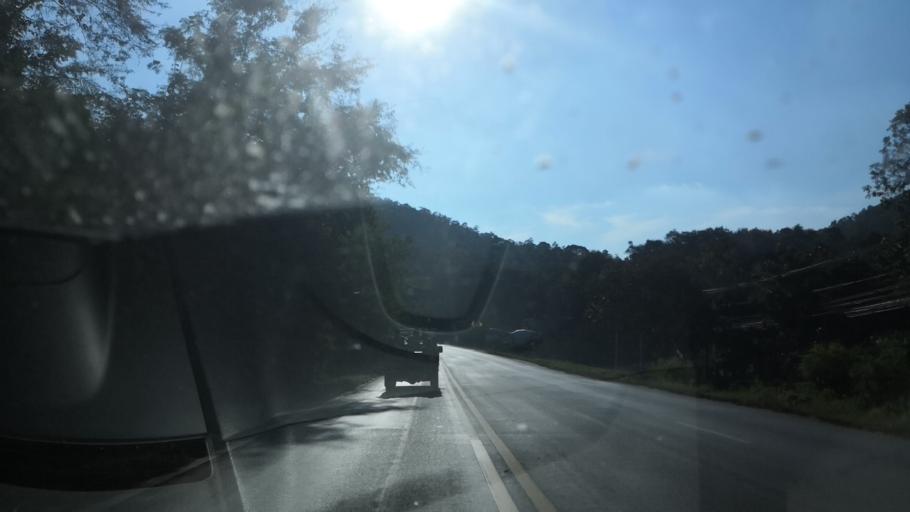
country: TH
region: Chiang Mai
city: Mae On
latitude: 18.9019
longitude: 99.1996
